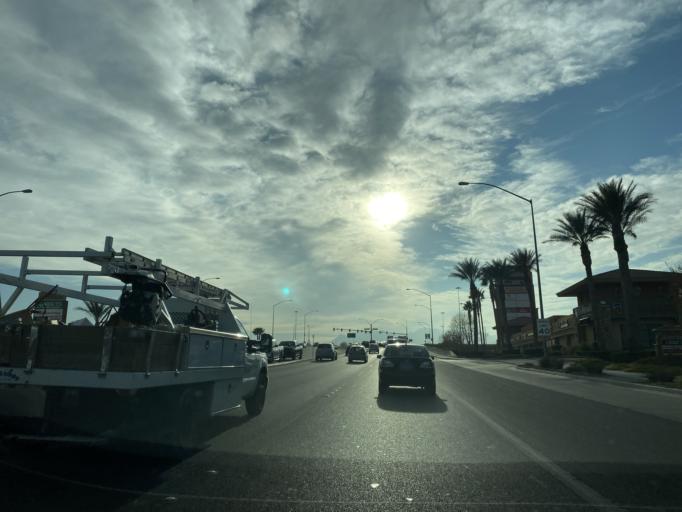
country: US
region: Nevada
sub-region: Clark County
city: Summerlin South
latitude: 36.3009
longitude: -115.2832
